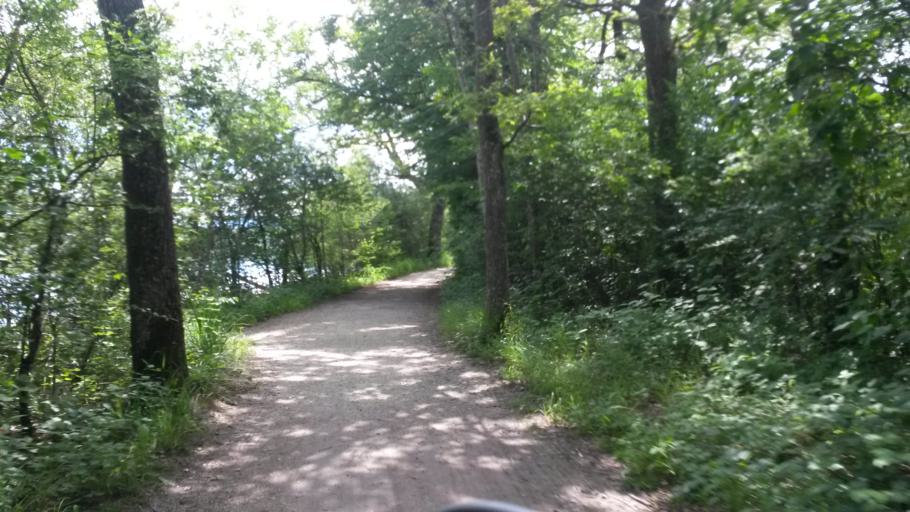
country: DE
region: Bavaria
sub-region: Upper Bavaria
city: Ubersee
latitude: 47.8609
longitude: 12.4790
